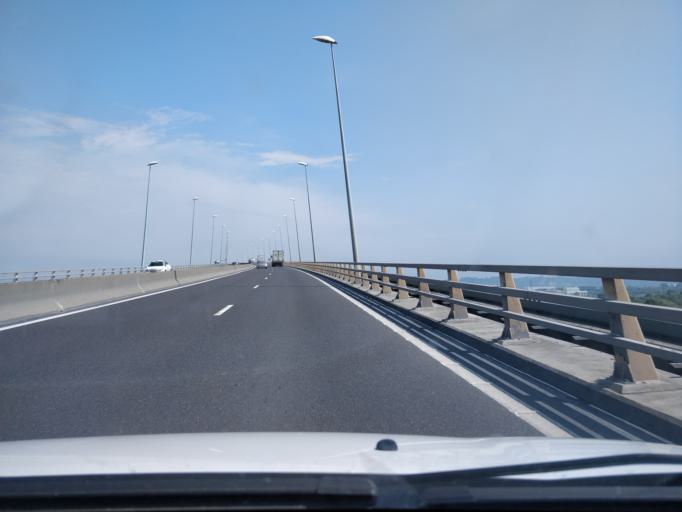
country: FR
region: Haute-Normandie
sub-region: Departement de la Seine-Maritime
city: Rogerville
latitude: 49.4604
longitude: 0.2740
